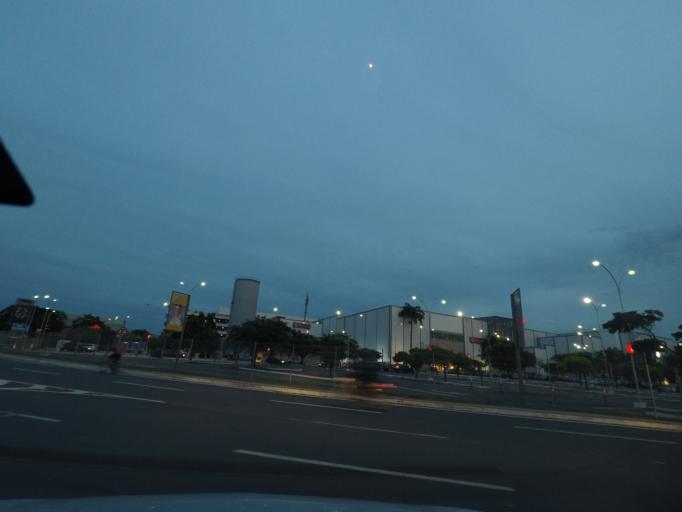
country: BR
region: Goias
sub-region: Goiania
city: Goiania
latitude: -16.7084
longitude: -49.2374
